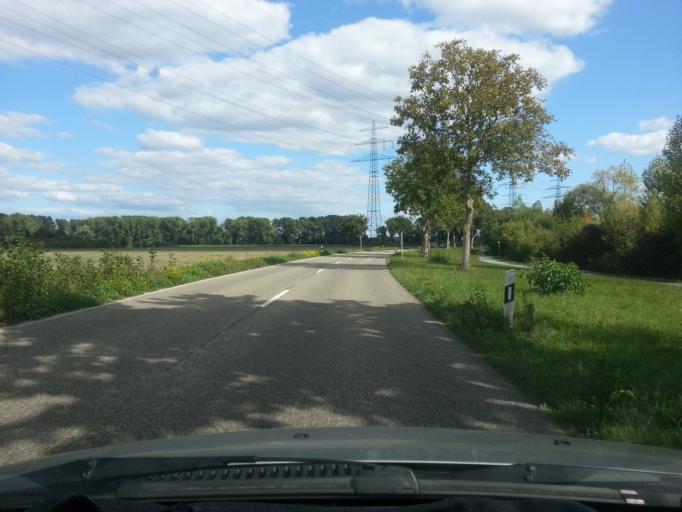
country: DE
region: Baden-Wuerttemberg
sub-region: Karlsruhe Region
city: Philippsburg
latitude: 49.2452
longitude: 8.4643
